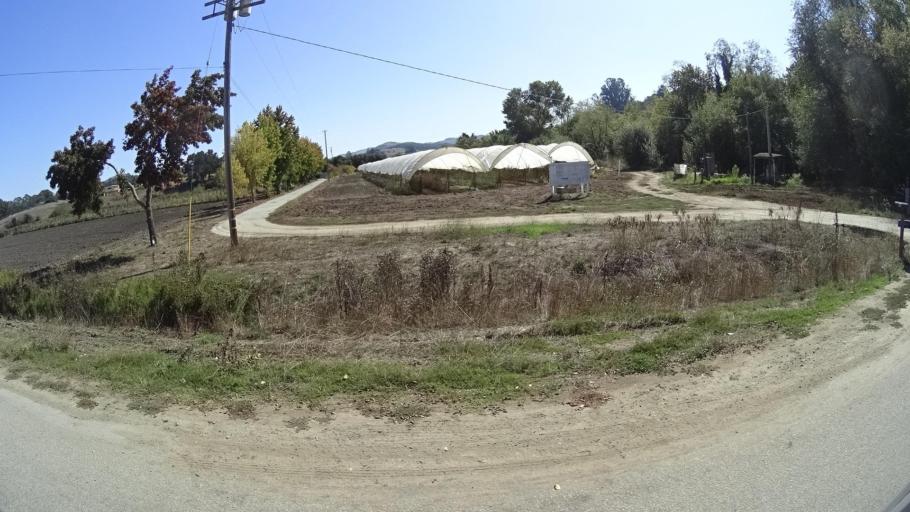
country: US
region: California
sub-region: San Benito County
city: Aromas
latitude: 36.8558
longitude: -121.6491
